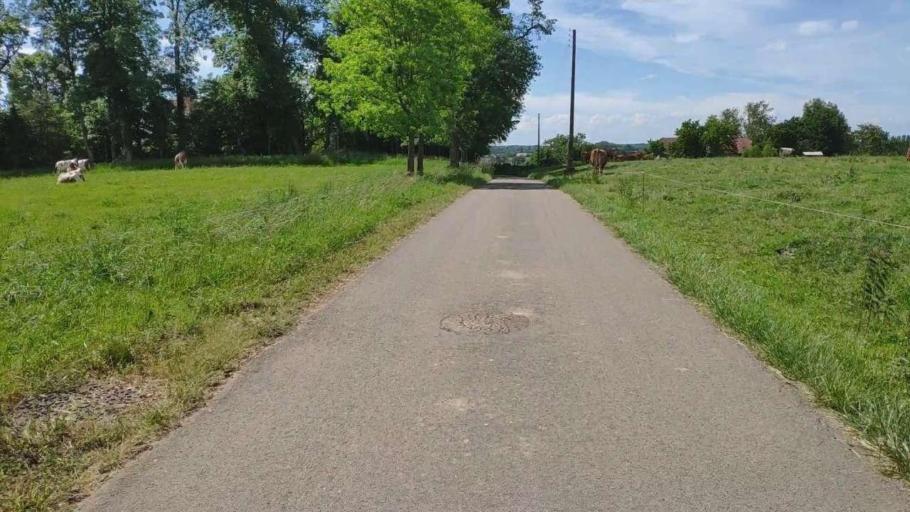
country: FR
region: Franche-Comte
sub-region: Departement du Jura
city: Bletterans
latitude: 46.7314
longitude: 5.5034
